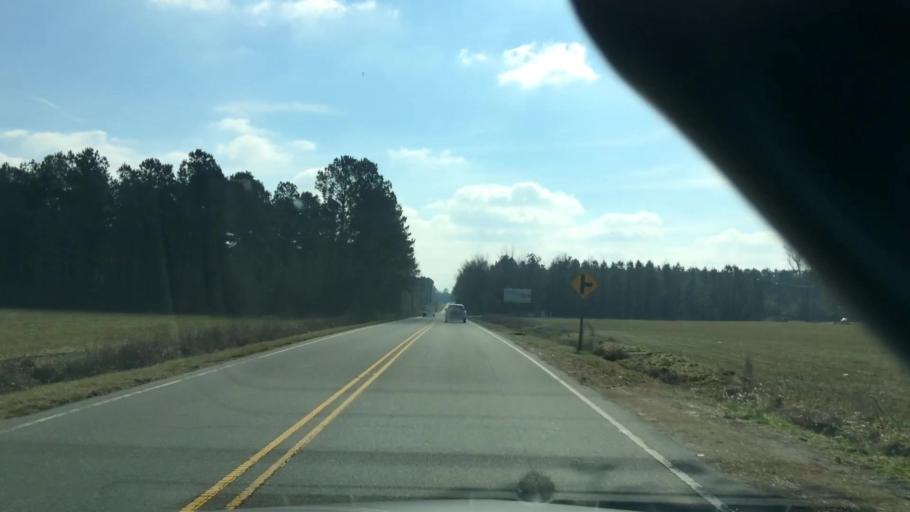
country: US
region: North Carolina
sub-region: Duplin County
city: Beulaville
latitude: 34.8538
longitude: -77.7979
